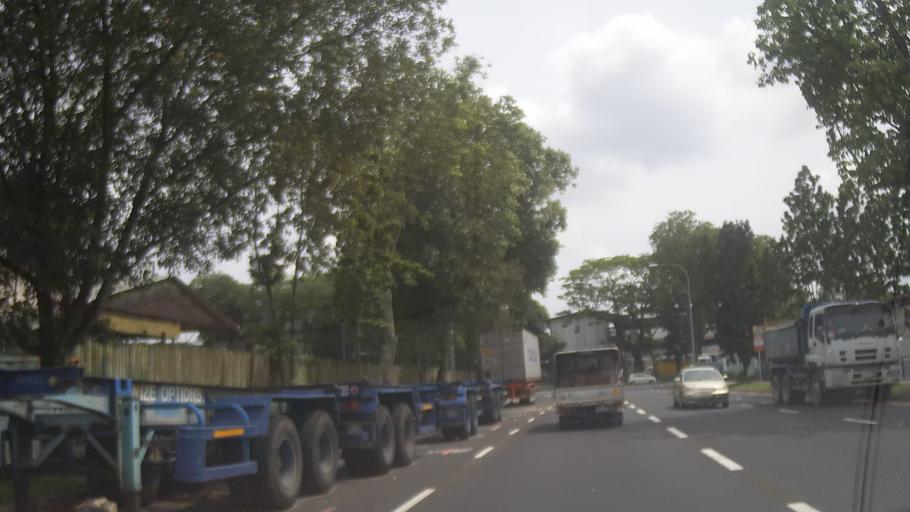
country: MY
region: Johor
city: Johor Bahru
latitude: 1.4173
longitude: 103.7502
